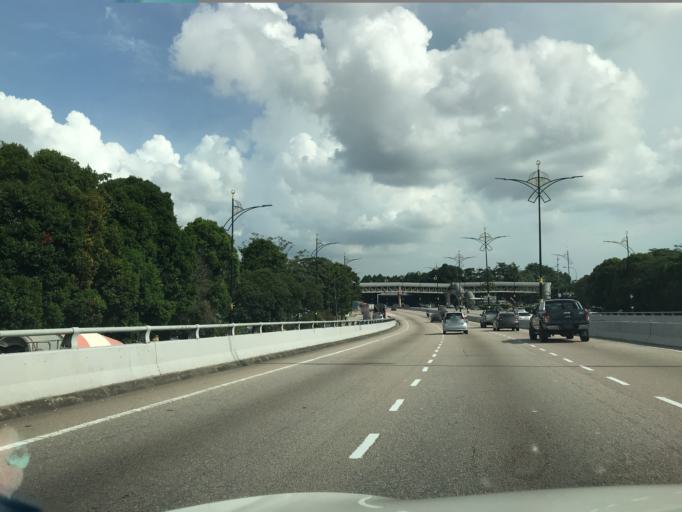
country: MY
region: Johor
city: Skudai
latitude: 1.5295
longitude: 103.6689
